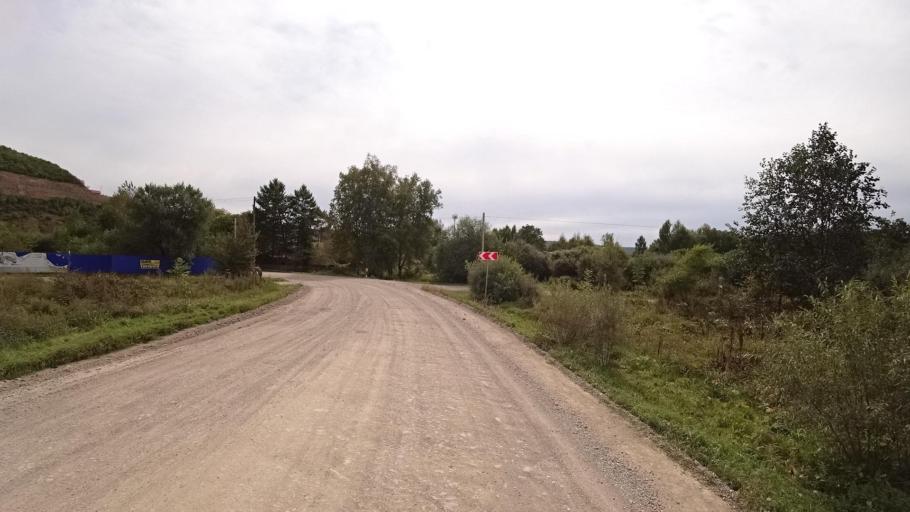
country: RU
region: Jewish Autonomous Oblast
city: Khingansk
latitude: 48.9906
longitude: 131.0527
